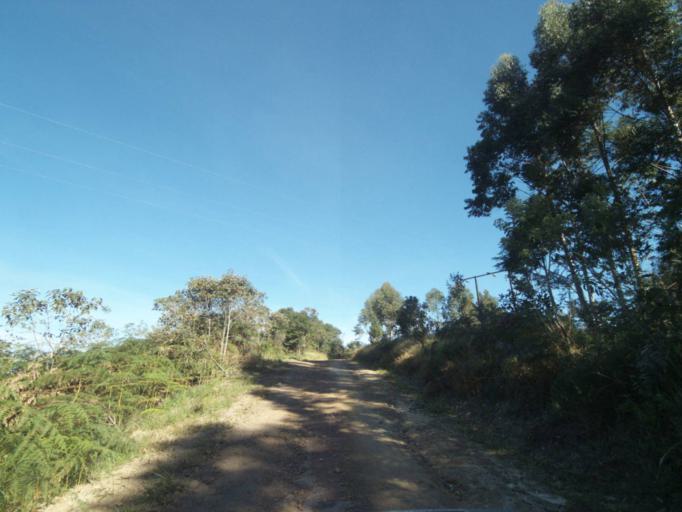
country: BR
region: Parana
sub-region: Tibagi
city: Tibagi
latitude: -24.5738
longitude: -50.4758
